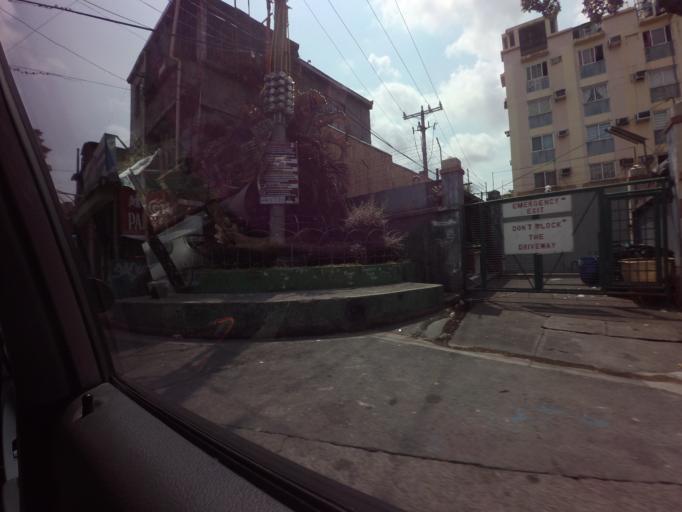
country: PH
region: Metro Manila
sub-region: San Juan
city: San Juan
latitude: 14.5974
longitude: 121.0225
